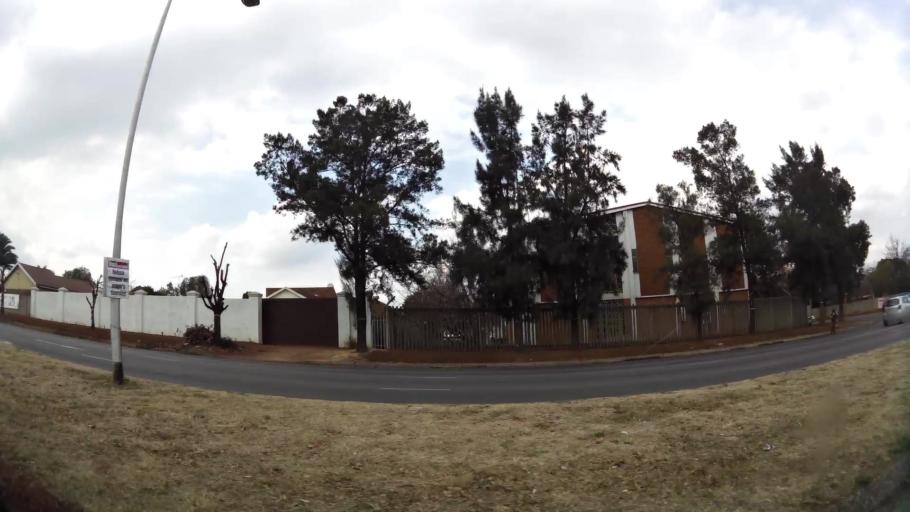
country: ZA
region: Gauteng
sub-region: Sedibeng District Municipality
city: Vanderbijlpark
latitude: -26.7263
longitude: 27.8372
